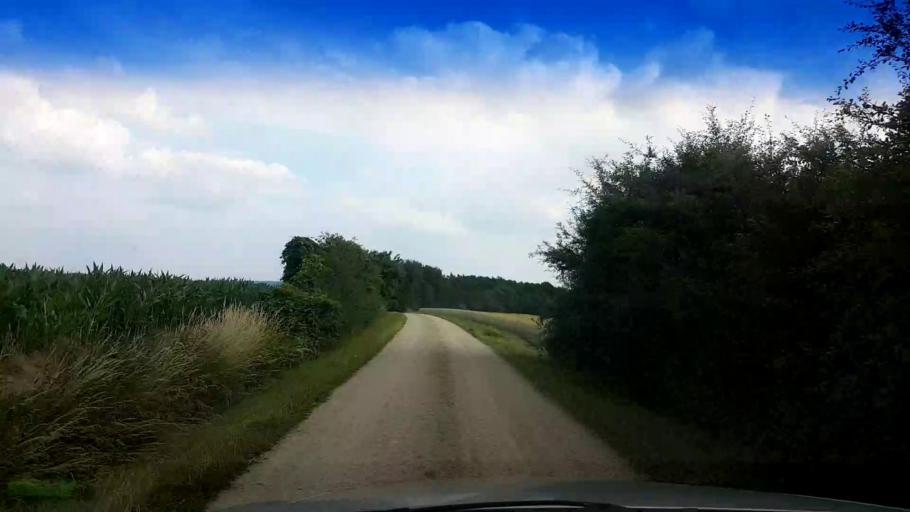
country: DE
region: Bavaria
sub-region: Upper Franconia
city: Walsdorf
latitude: 49.8785
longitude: 10.8135
